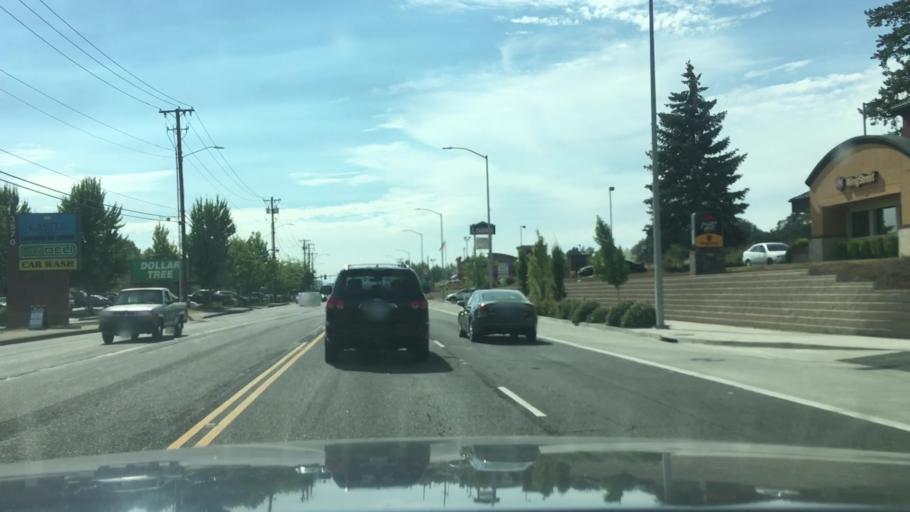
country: US
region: Oregon
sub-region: Lane County
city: Eugene
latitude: 44.0481
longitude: -123.1450
